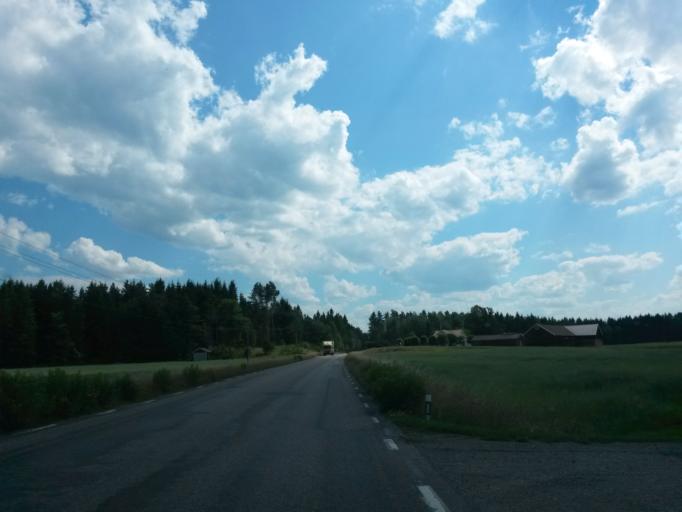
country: SE
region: Vaestra Goetaland
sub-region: Essunga Kommun
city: Nossebro
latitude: 58.1738
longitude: 12.7411
